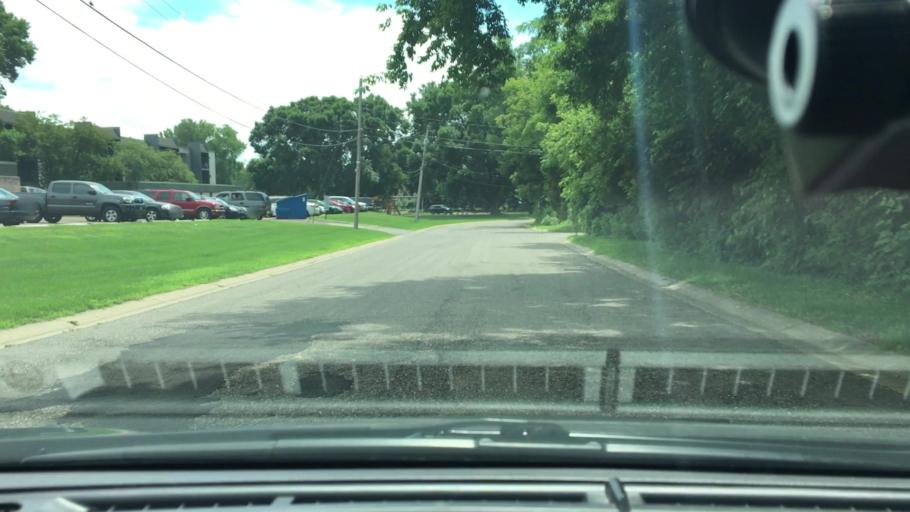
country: US
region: Minnesota
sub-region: Hennepin County
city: New Hope
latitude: 45.0066
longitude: -93.4057
